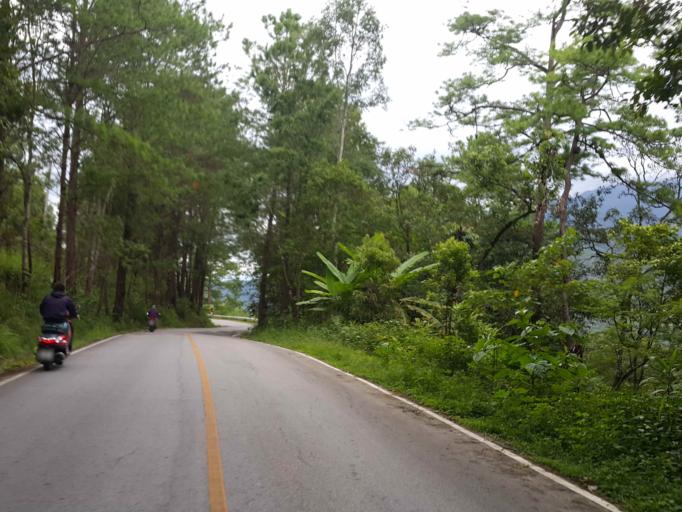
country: TH
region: Chiang Mai
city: Mae Chaem
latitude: 18.5154
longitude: 98.4541
